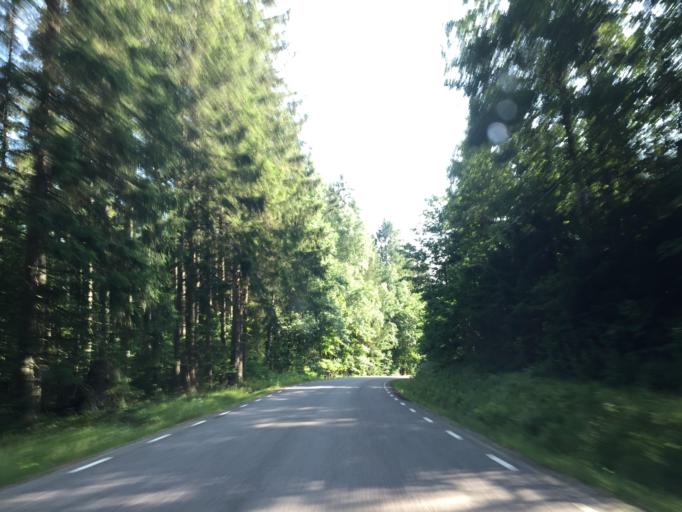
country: SE
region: Vaestra Goetaland
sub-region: Trollhattan
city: Trollhattan
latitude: 58.2639
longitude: 12.2325
